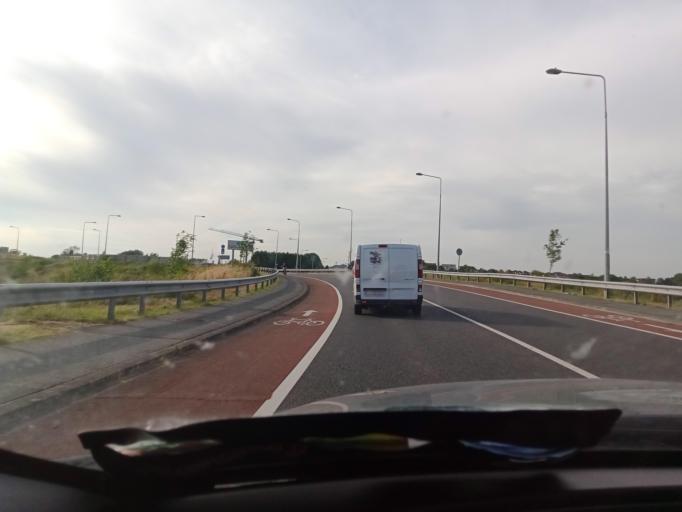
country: IE
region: Ulster
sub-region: An Cabhan
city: Cavan
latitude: 53.9881
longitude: -7.3509
